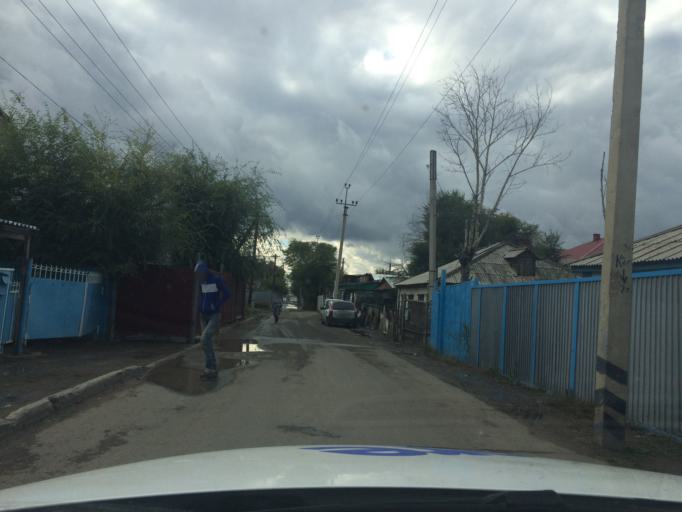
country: KZ
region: Astana Qalasy
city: Astana
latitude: 51.1866
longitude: 71.4002
